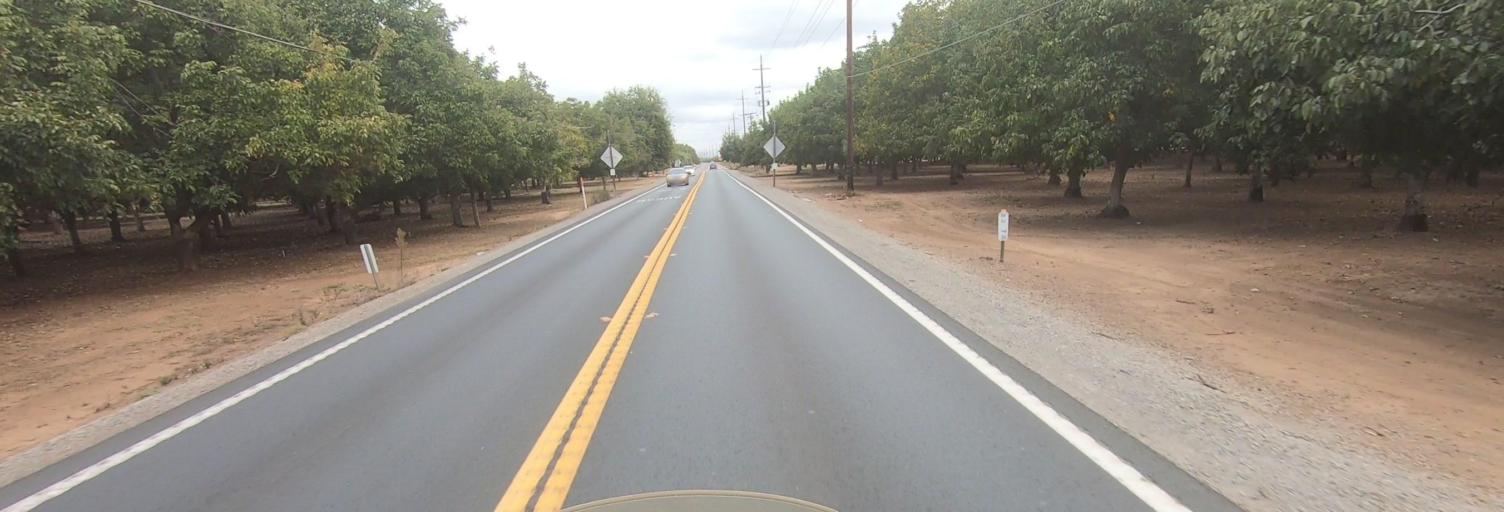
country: US
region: California
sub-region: San Joaquin County
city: Linden
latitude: 38.0015
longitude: -121.1466
